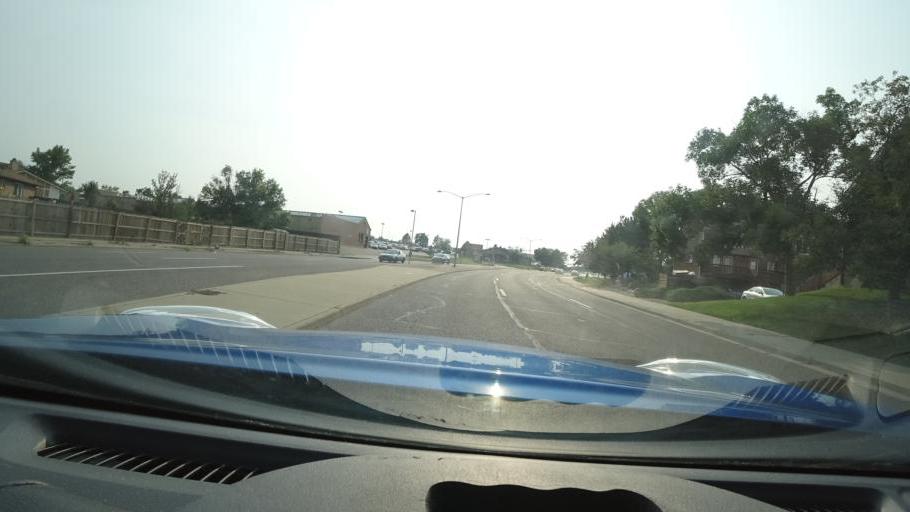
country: US
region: Colorado
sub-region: Adams County
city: Aurora
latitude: 39.6732
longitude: -104.7874
